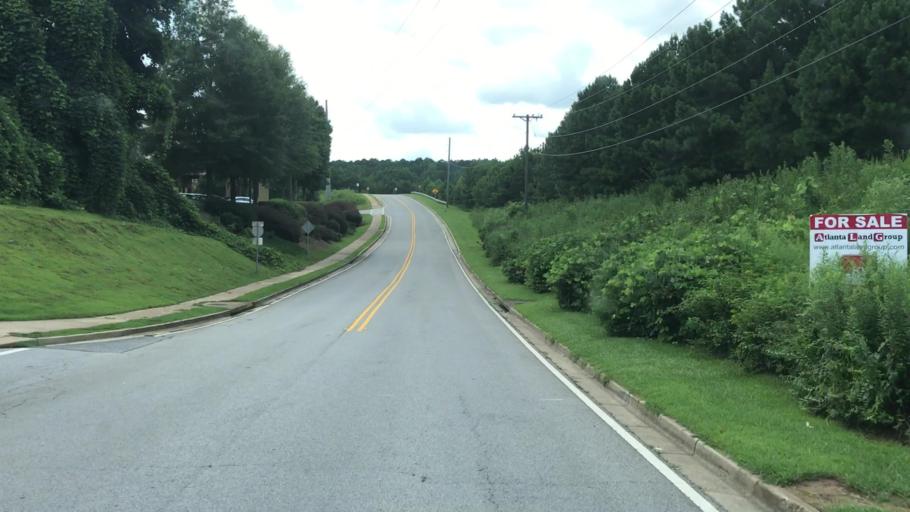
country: US
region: Georgia
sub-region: Gwinnett County
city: Suwanee
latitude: 34.0258
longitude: -84.0510
